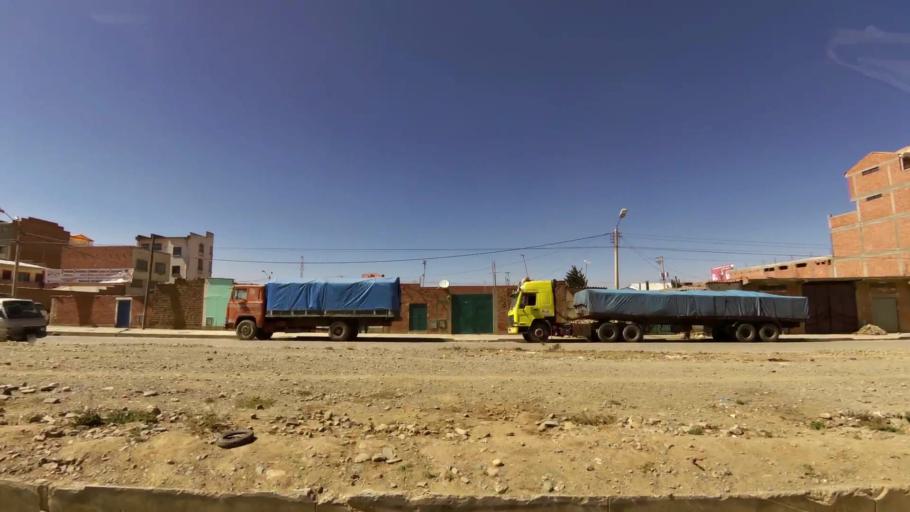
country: BO
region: La Paz
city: La Paz
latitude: -16.5366
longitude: -68.1937
